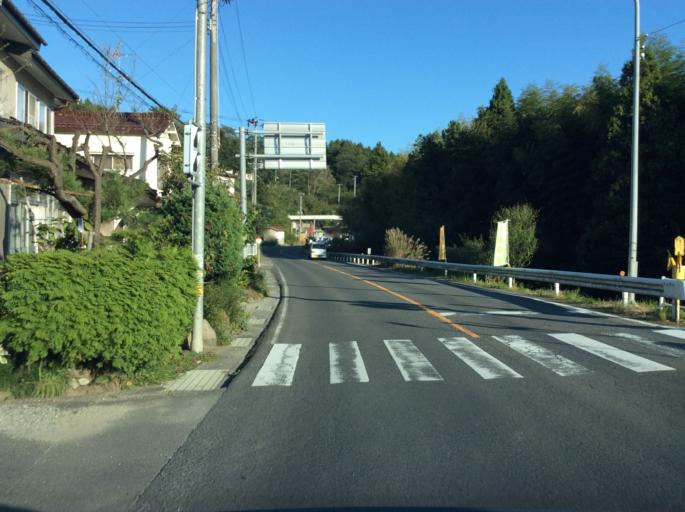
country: JP
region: Fukushima
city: Koriyama
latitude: 37.4184
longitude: 140.4294
